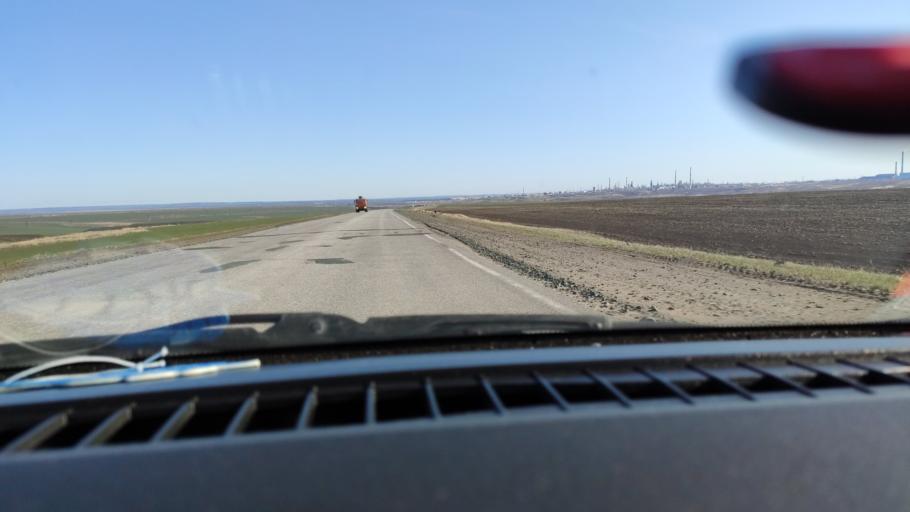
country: RU
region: Samara
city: Varlamovo
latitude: 53.0369
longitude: 48.3372
